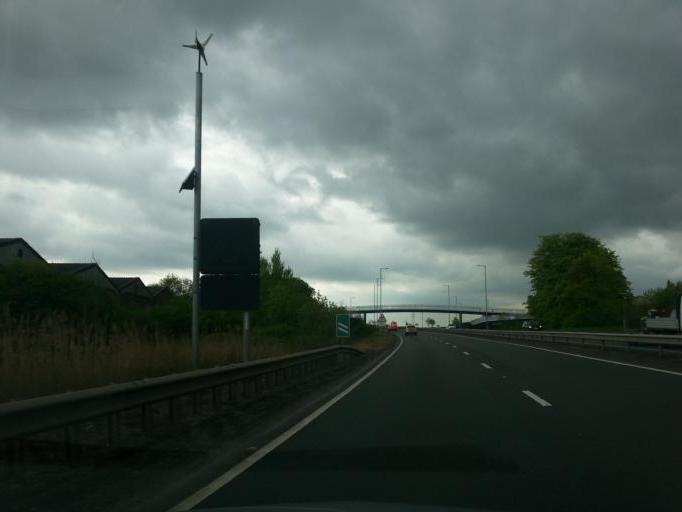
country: GB
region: England
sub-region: Peterborough
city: Thorney
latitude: 52.6269
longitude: -0.1057
